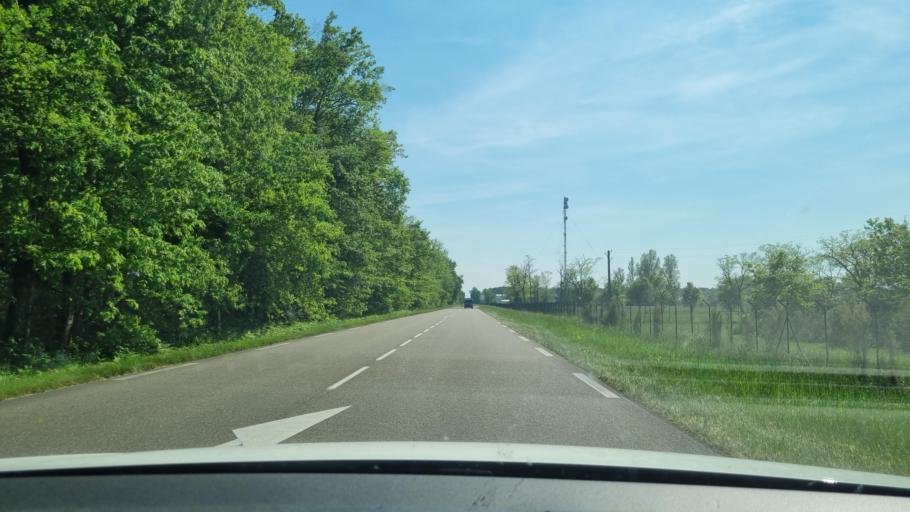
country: FR
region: Aquitaine
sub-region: Departement des Landes
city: Roquefort
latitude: 44.1886
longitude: -0.2742
